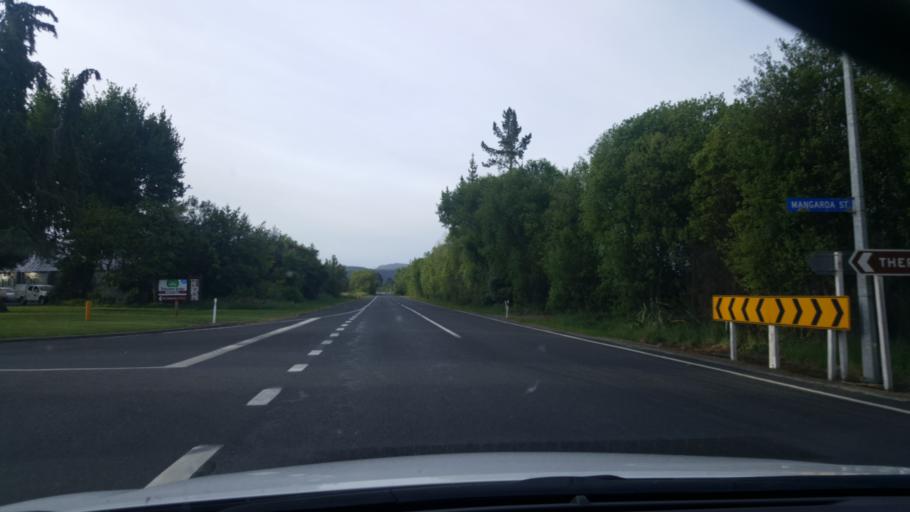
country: NZ
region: Waikato
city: Turangi
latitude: -38.9692
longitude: 175.7689
